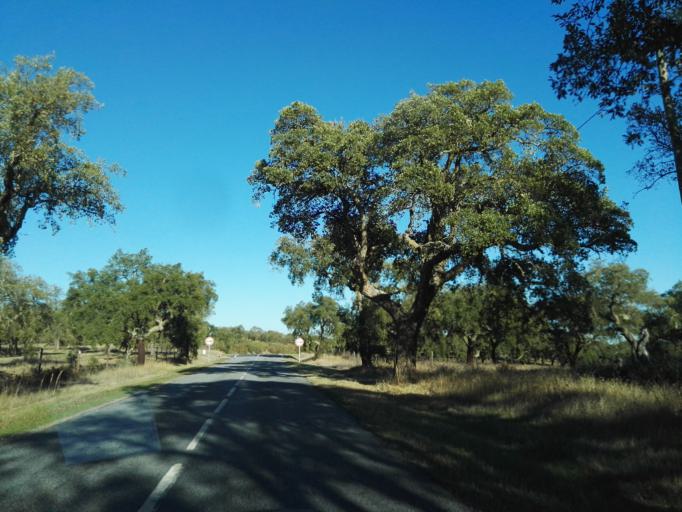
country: PT
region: Evora
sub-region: Evora
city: Evora
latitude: 38.7032
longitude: -7.8050
